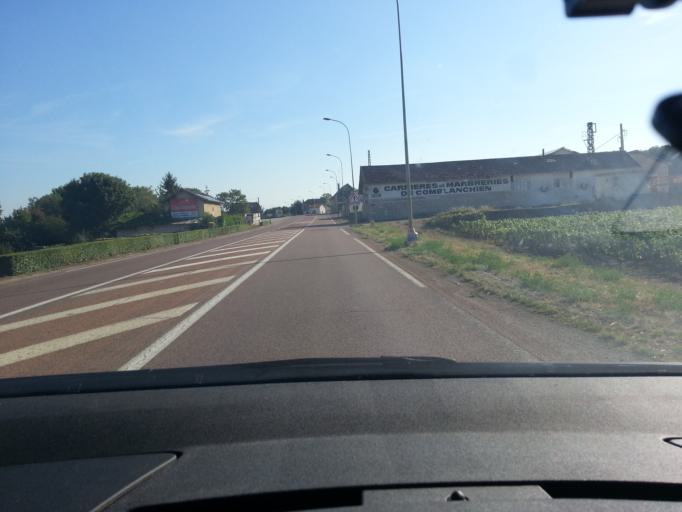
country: FR
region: Bourgogne
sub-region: Departement de la Cote-d'Or
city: Nuits-Saint-Georges
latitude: 47.1004
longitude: 4.9156
